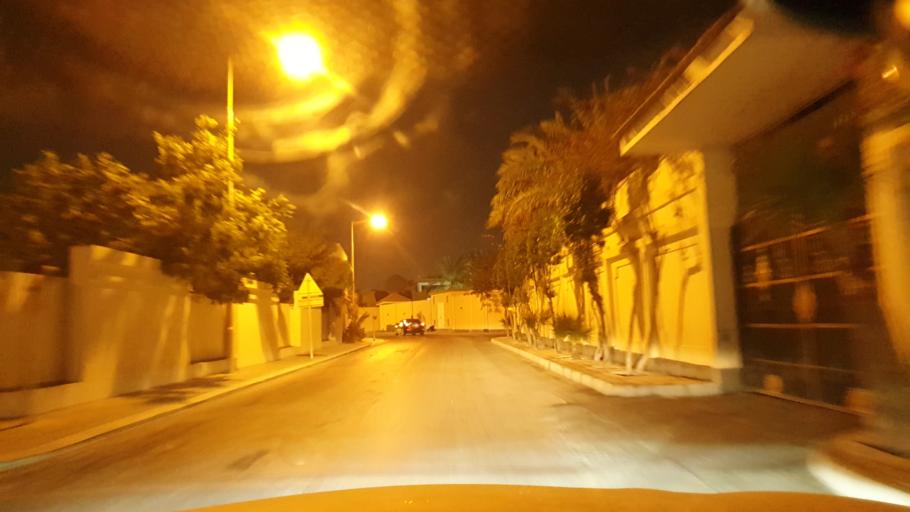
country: BH
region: Manama
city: Jidd Hafs
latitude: 26.1970
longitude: 50.4931
